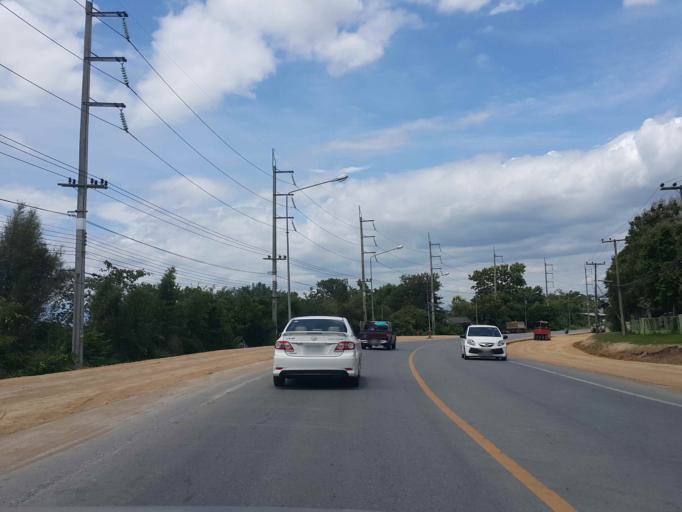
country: TH
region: Lamphun
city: Ban Hong
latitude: 18.3213
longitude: 98.8178
